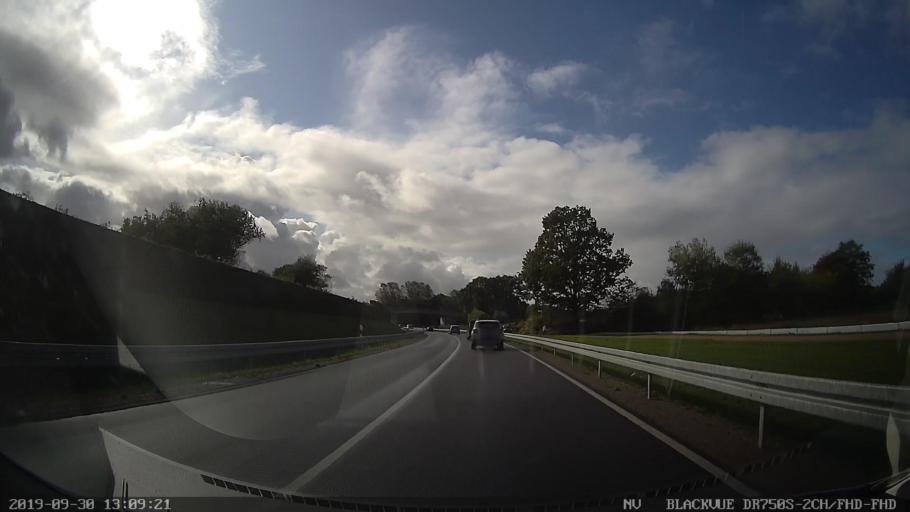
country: DE
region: Schleswig-Holstein
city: Kummerfeld
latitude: 53.6783
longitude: 9.7885
